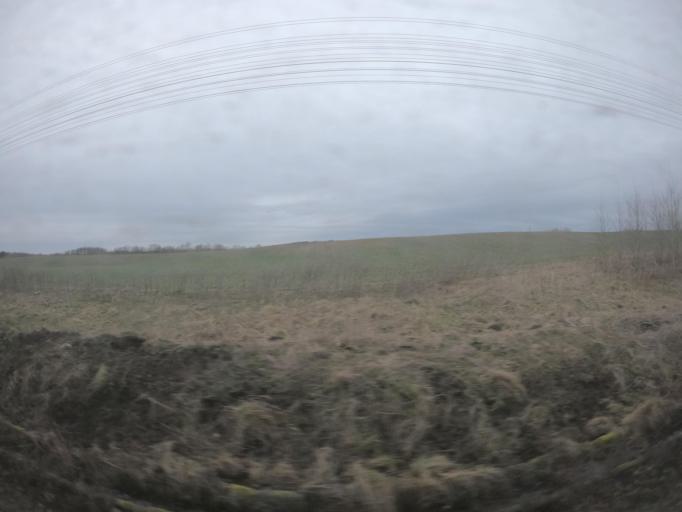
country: PL
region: West Pomeranian Voivodeship
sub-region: Powiat szczecinecki
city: Szczecinek
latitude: 53.6785
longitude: 16.6792
